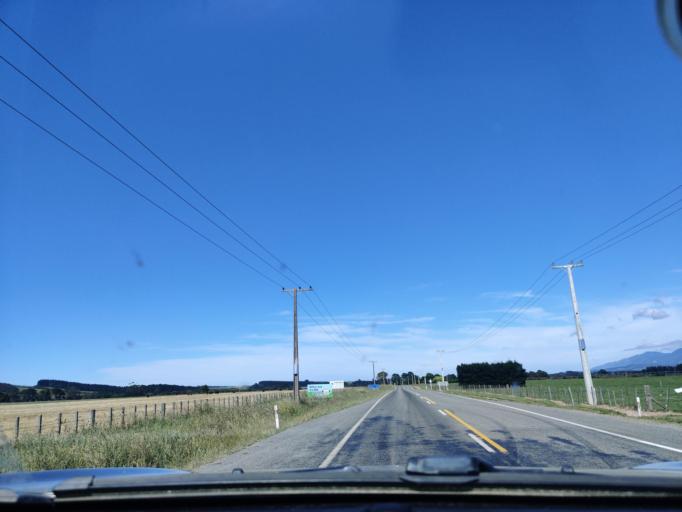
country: NZ
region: Wellington
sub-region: South Wairarapa District
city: Waipawa
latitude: -41.3063
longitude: 175.2732
